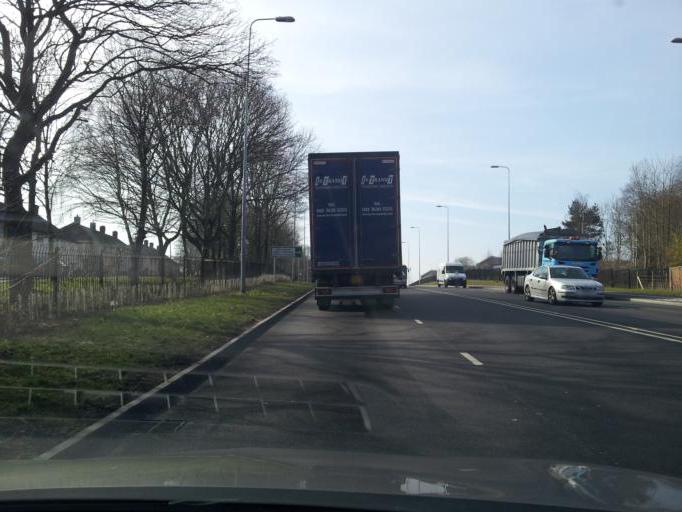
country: GB
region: England
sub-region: Nottinghamshire
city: Ruddington
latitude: 52.9135
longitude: -1.1793
